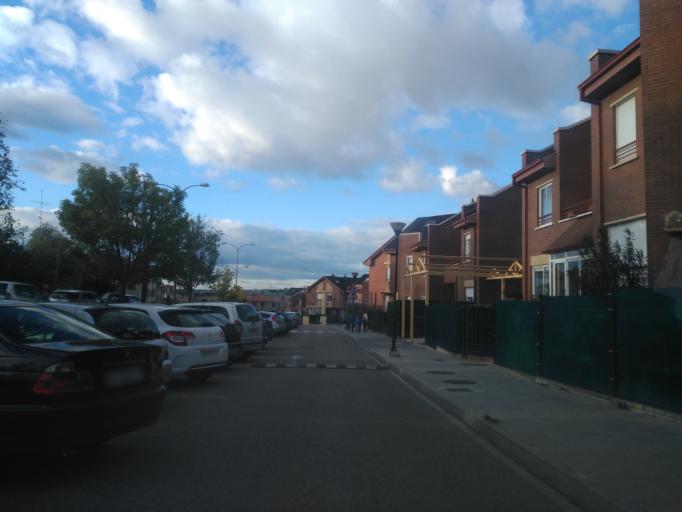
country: ES
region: Castille and Leon
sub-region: Provincia de Salamanca
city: Villamayor
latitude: 40.9967
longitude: -5.6935
